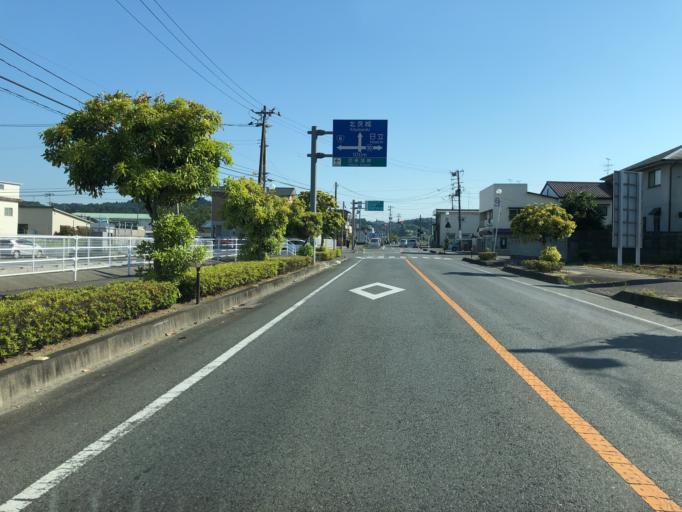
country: JP
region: Ibaraki
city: Kitaibaraki
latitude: 36.8912
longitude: 140.7667
